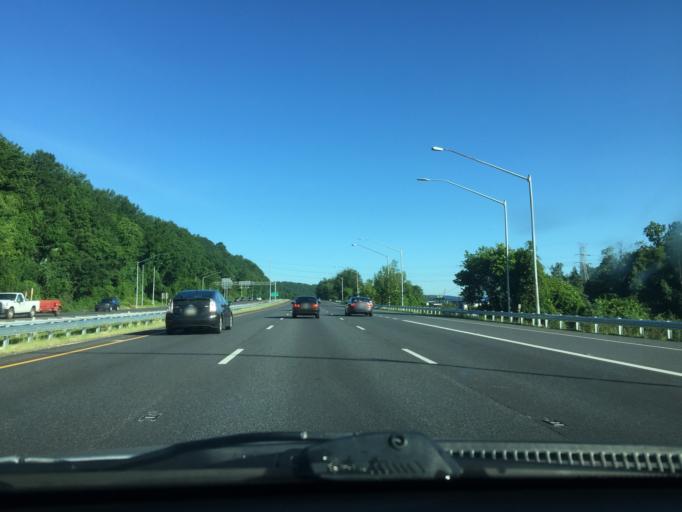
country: US
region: Maryland
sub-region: Baltimore County
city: Mays Chapel
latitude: 39.4559
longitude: -76.6483
